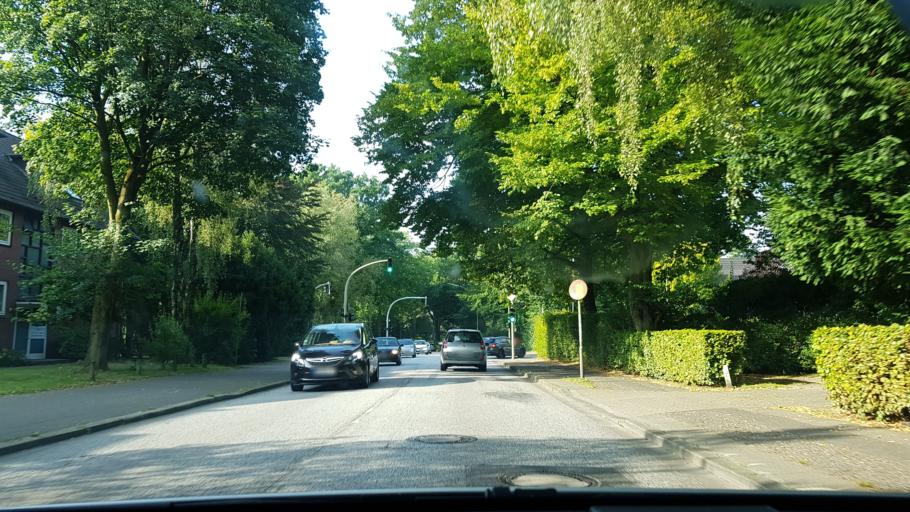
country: DE
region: Hamburg
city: Farmsen-Berne
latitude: 53.6335
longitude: 10.1453
